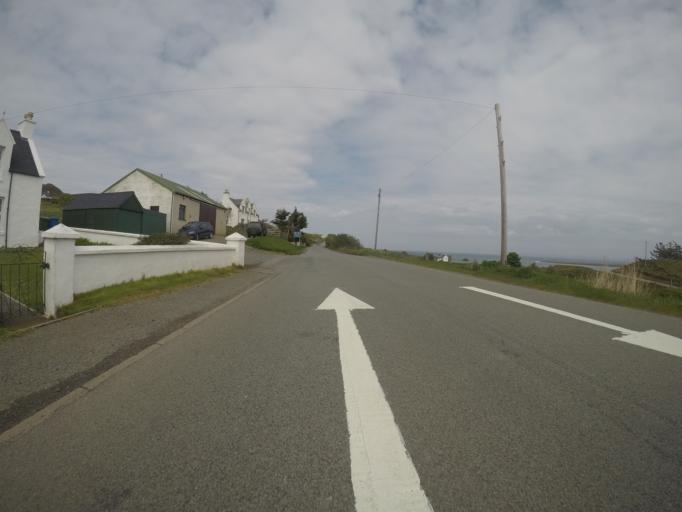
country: GB
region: Scotland
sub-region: Highland
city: Portree
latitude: 57.6331
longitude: -6.2413
